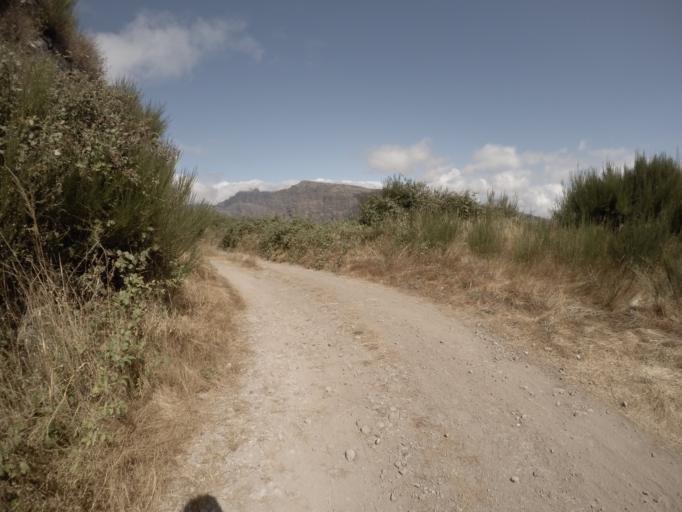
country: PT
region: Madeira
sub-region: Camara de Lobos
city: Curral das Freiras
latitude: 32.7097
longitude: -16.9876
